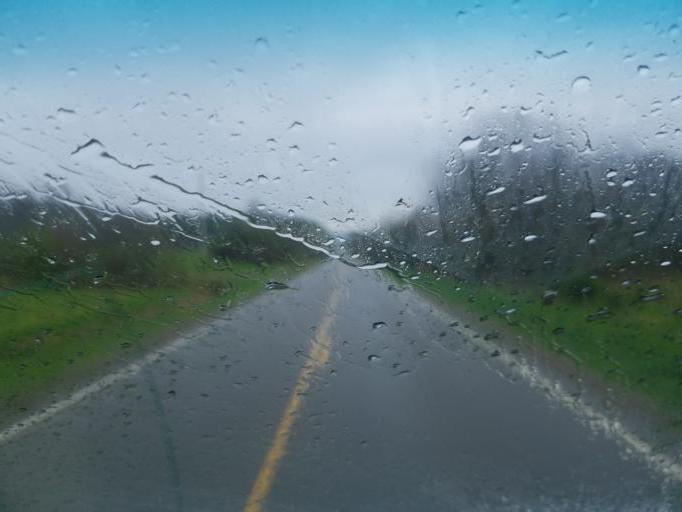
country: US
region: New York
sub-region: Allegany County
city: Friendship
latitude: 42.1839
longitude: -78.0837
